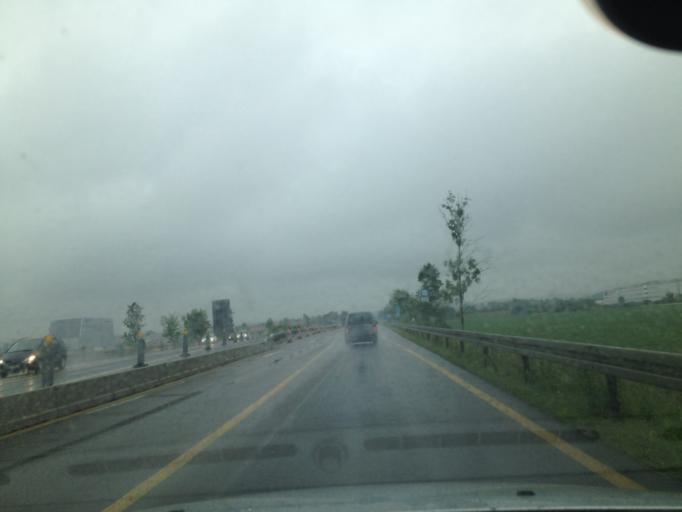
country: DE
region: Hesse
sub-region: Regierungsbezirk Darmstadt
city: Langenselbold
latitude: 50.1732
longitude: 9.0160
